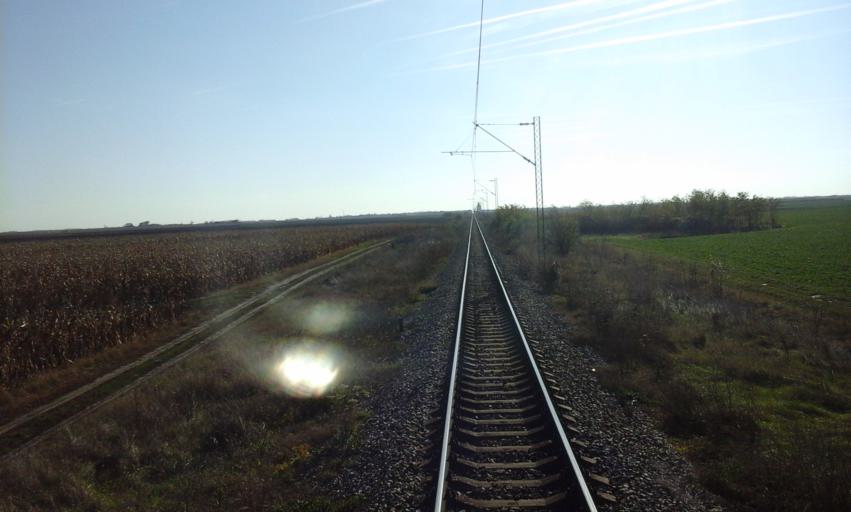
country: RS
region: Autonomna Pokrajina Vojvodina
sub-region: Severnobacki Okrug
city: Subotica
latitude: 45.9793
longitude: 19.6744
